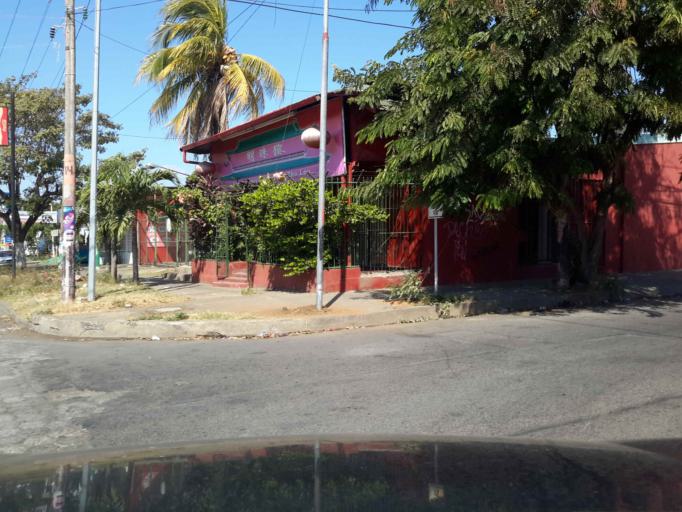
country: NI
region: Managua
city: Ciudad Sandino
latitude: 12.1499
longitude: -86.3046
